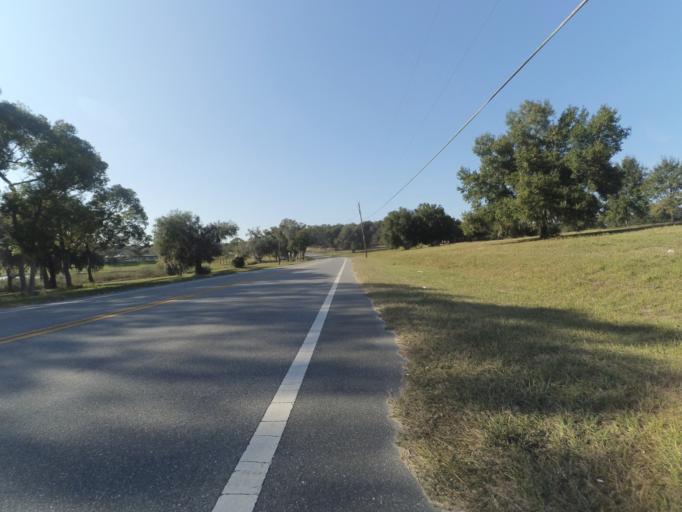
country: US
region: Florida
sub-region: Lake County
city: Umatilla
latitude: 28.9669
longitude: -81.6502
